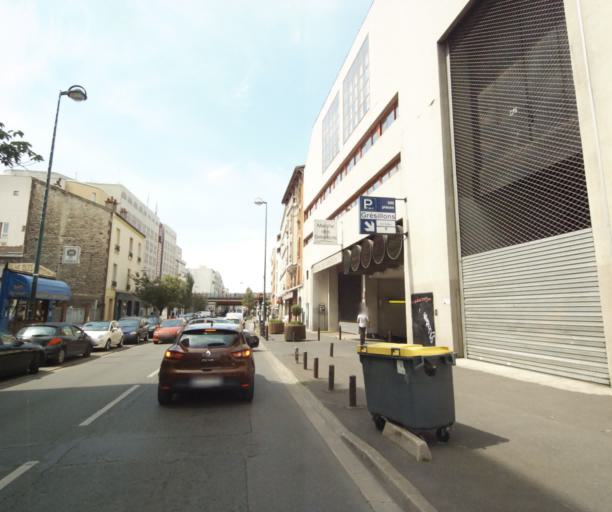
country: FR
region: Ile-de-France
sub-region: Departement des Hauts-de-Seine
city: Asnieres-sur-Seine
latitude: 48.9140
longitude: 2.2994
